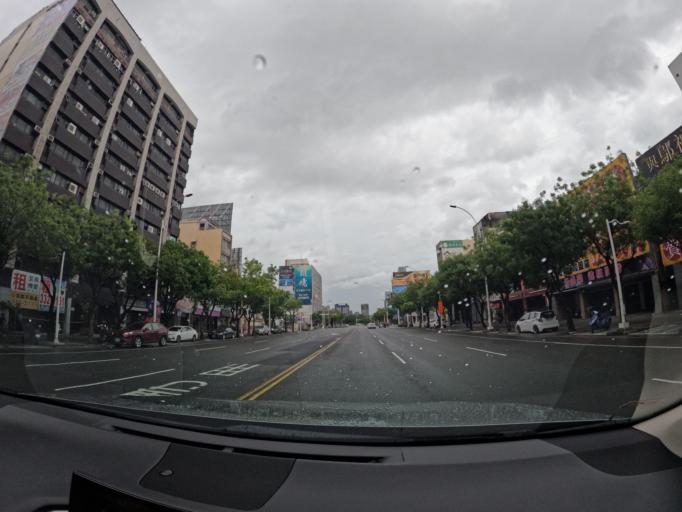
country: TW
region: Kaohsiung
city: Kaohsiung
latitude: 22.6205
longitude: 120.3020
